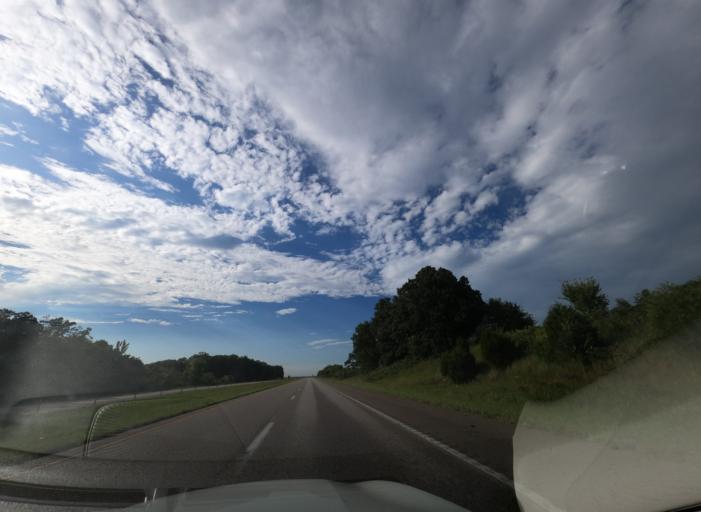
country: US
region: Missouri
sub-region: Jefferson County
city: Crystal City
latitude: 38.0467
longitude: -90.2674
